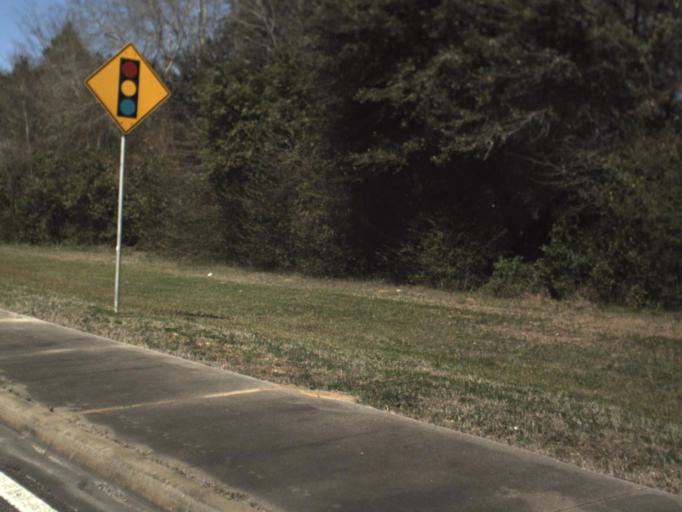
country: US
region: Florida
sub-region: Jackson County
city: Graceville
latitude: 30.9475
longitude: -85.4013
